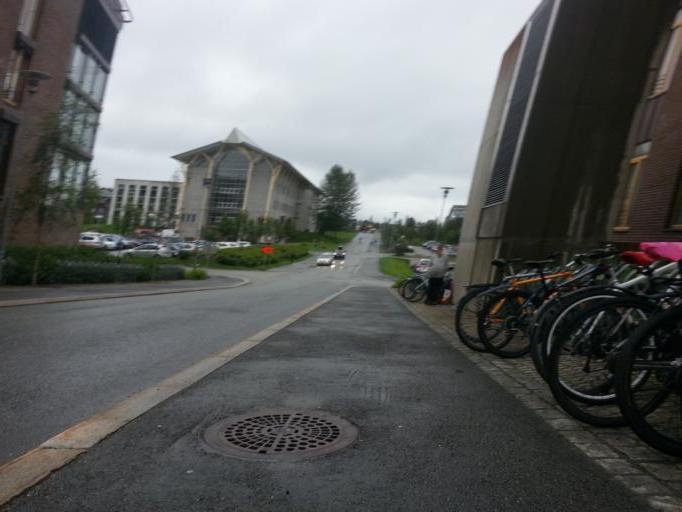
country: NO
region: Troms
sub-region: Tromso
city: Tromso
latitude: 69.6815
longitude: 18.9712
